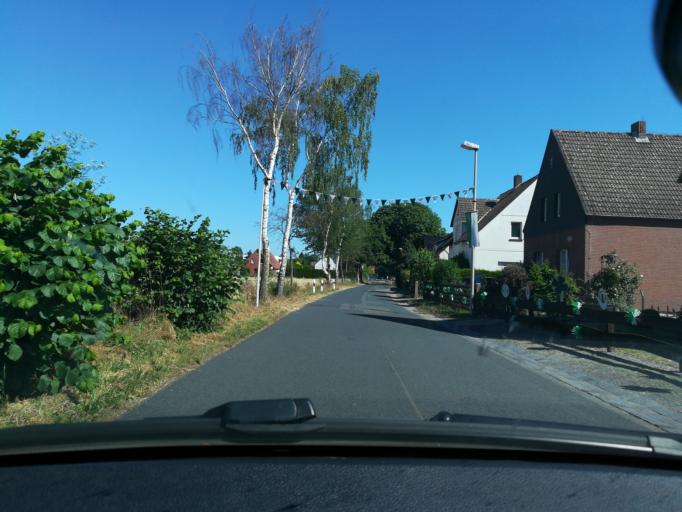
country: DE
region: North Rhine-Westphalia
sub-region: Regierungsbezirk Detmold
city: Minden
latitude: 52.3122
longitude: 8.9285
